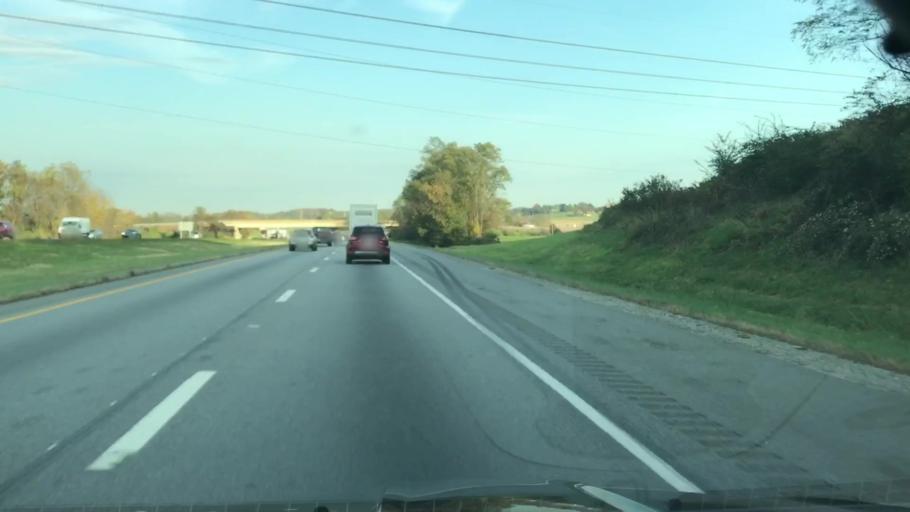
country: US
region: Pennsylvania
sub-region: Cumberland County
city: Schlusser
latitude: 40.2426
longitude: -77.1051
